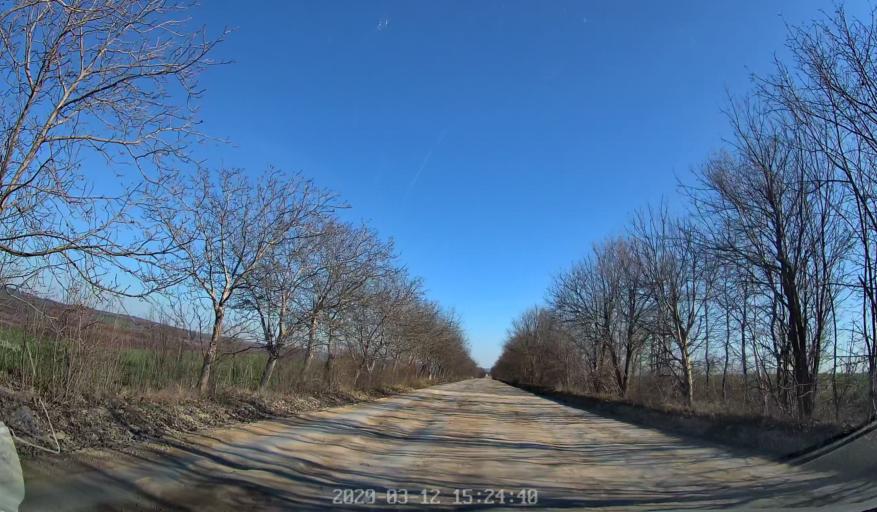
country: MD
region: Chisinau
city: Ciorescu
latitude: 47.1856
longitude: 28.9145
